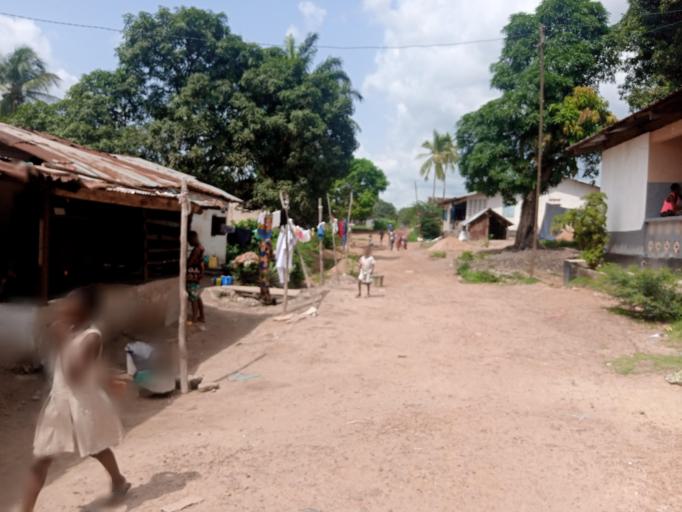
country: SL
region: Southern Province
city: Bo
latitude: 7.9769
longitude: -11.7353
